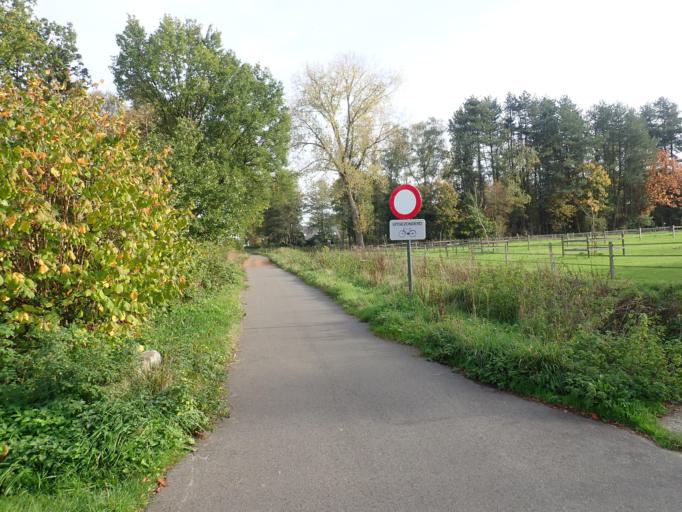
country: BE
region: Flanders
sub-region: Provincie Oost-Vlaanderen
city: Stekene
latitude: 51.1764
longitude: 4.0828
